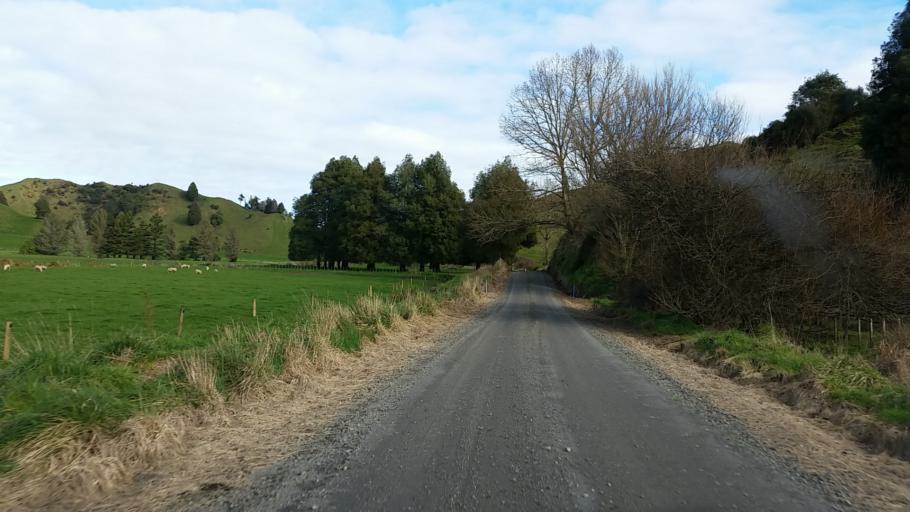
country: NZ
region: Taranaki
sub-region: South Taranaki District
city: Eltham
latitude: -39.2554
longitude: 174.5291
